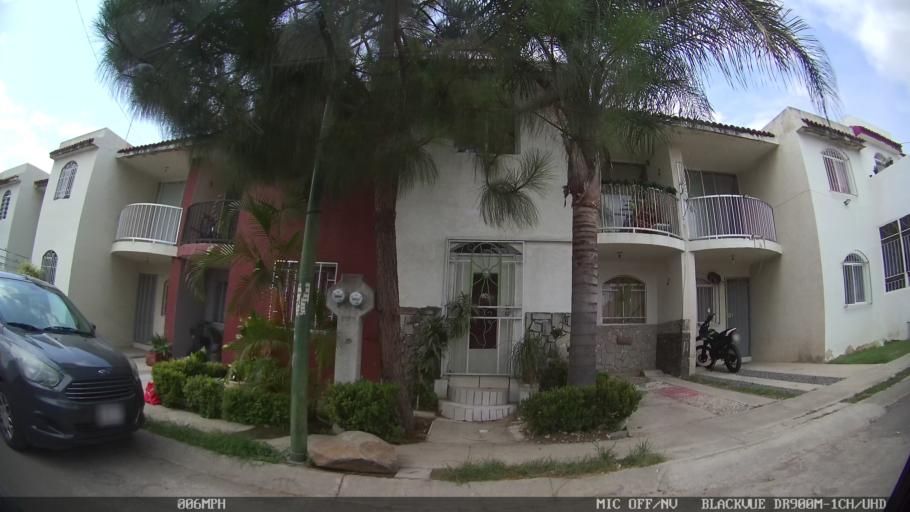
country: MX
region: Jalisco
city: Coyula
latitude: 20.6391
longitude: -103.2154
